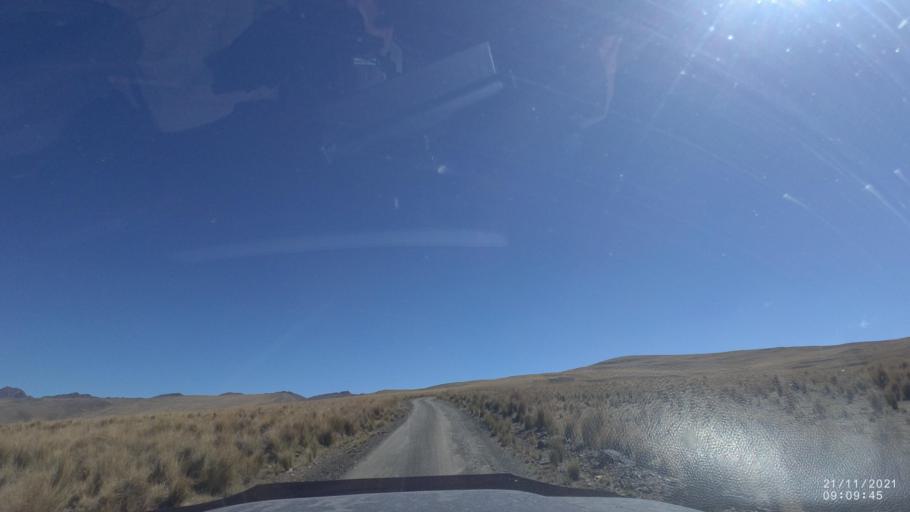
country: BO
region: Cochabamba
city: Cochabamba
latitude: -17.1577
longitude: -66.2603
